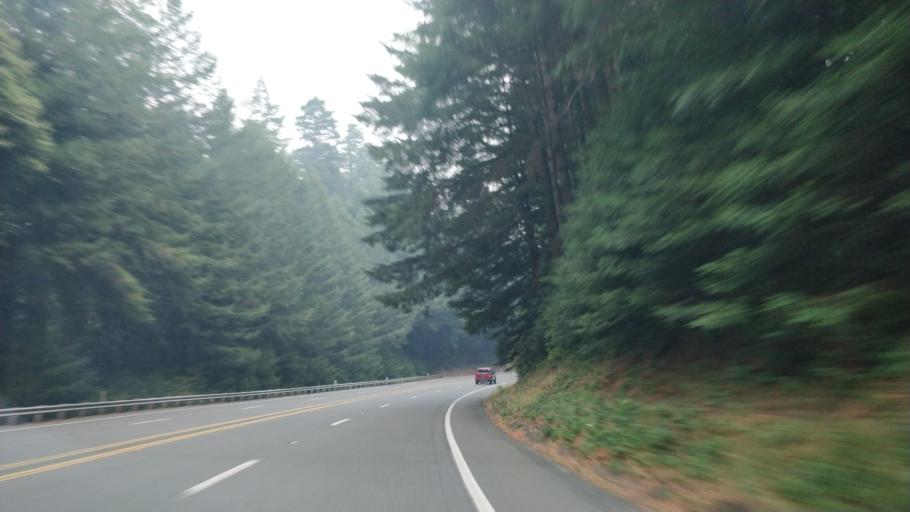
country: US
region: California
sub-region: Humboldt County
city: Rio Dell
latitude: 40.3957
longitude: -123.9372
